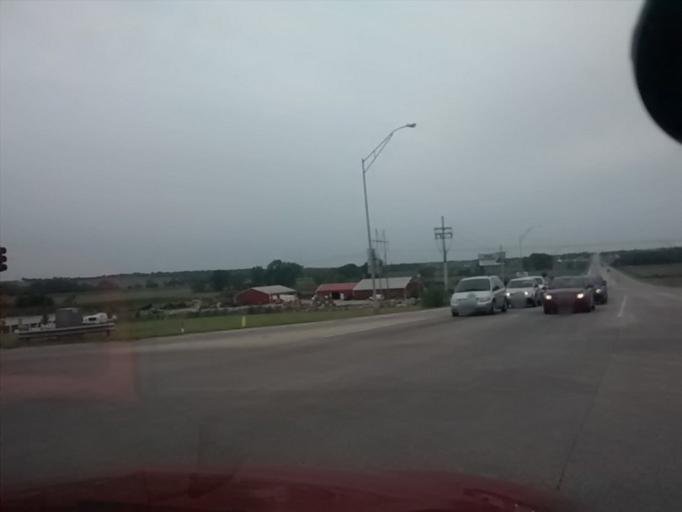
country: US
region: Nebraska
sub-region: Sarpy County
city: Offutt Air Force Base
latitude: 41.1619
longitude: -95.9669
